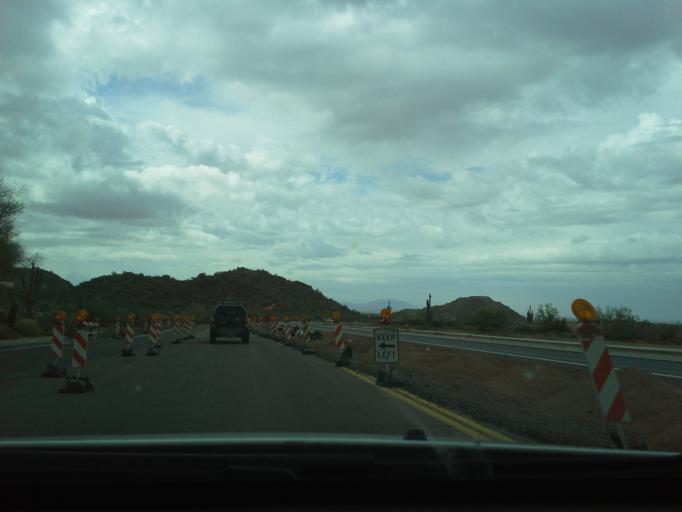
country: US
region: Arizona
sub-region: Pinal County
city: Apache Junction
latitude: 33.4569
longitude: -111.6324
